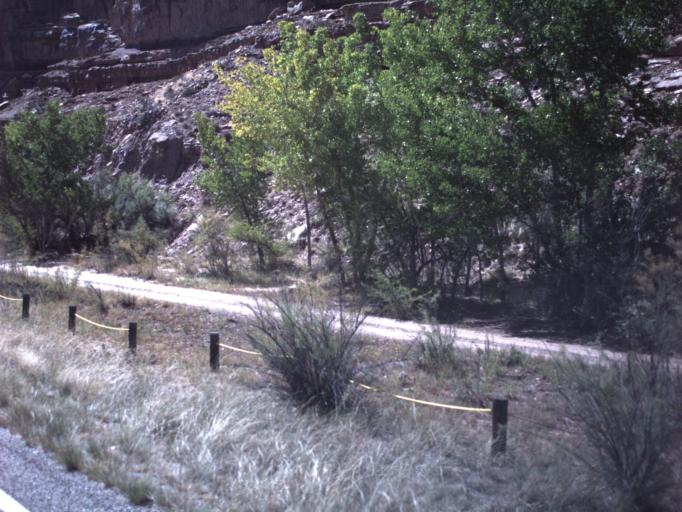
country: US
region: Utah
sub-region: Grand County
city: Moab
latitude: 38.5354
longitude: -109.6060
